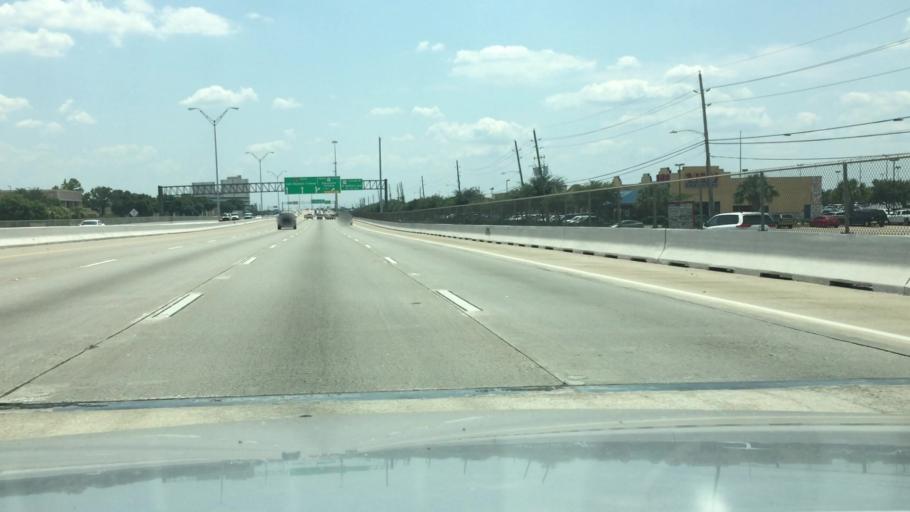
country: US
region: Texas
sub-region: Fort Bend County
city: Meadows Place
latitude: 29.6845
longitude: -95.5586
